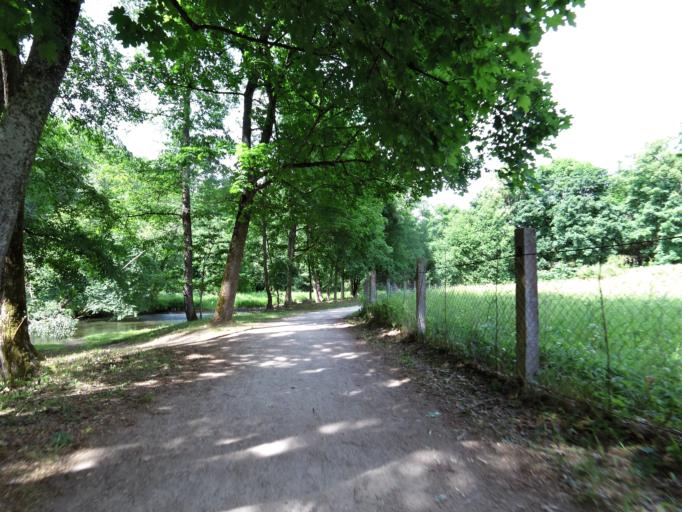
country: LT
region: Vilnius County
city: Rasos
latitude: 54.6875
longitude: 25.3531
